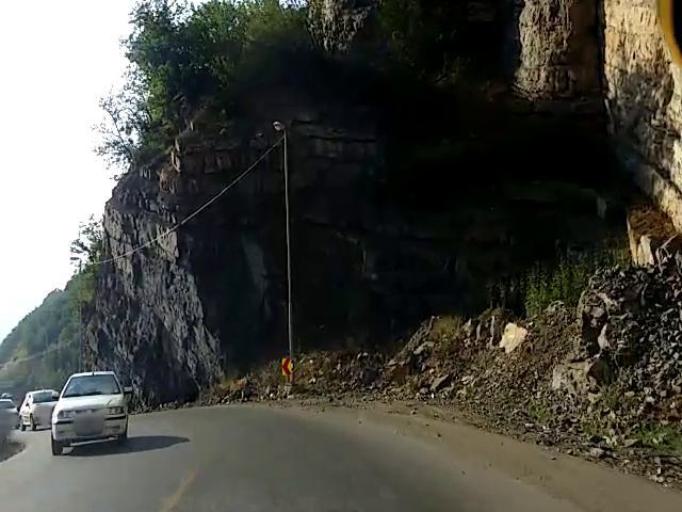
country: IR
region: Mazandaran
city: Chalus
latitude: 36.2547
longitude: 51.2784
